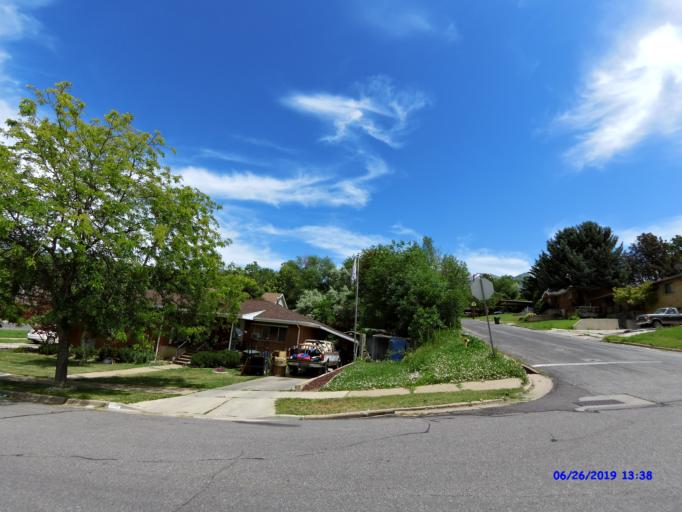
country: US
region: Utah
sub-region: Weber County
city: South Ogden
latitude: 41.2037
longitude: -111.9639
